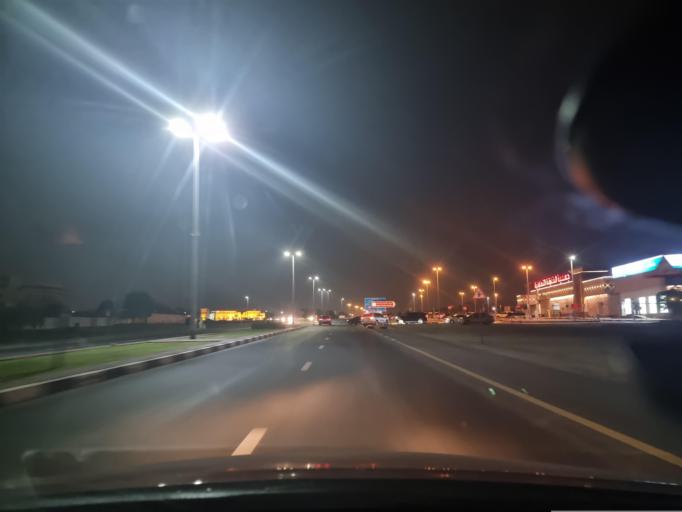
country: AE
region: Ash Shariqah
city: Sharjah
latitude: 25.3496
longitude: 55.4603
